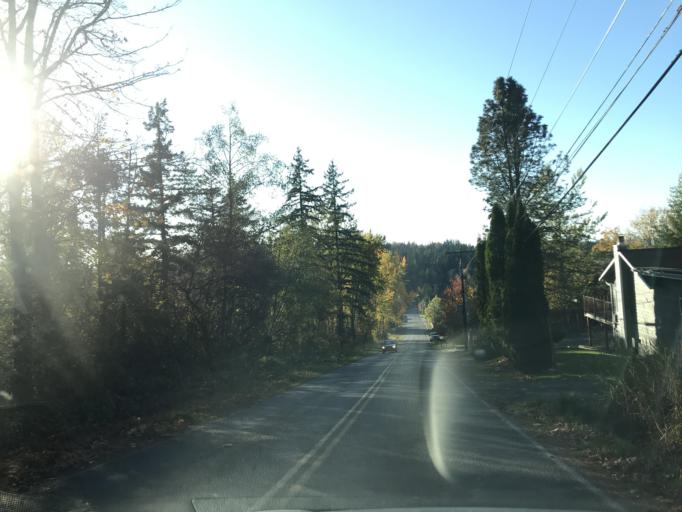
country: US
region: Washington
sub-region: Whatcom County
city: Geneva
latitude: 48.7769
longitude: -122.4002
